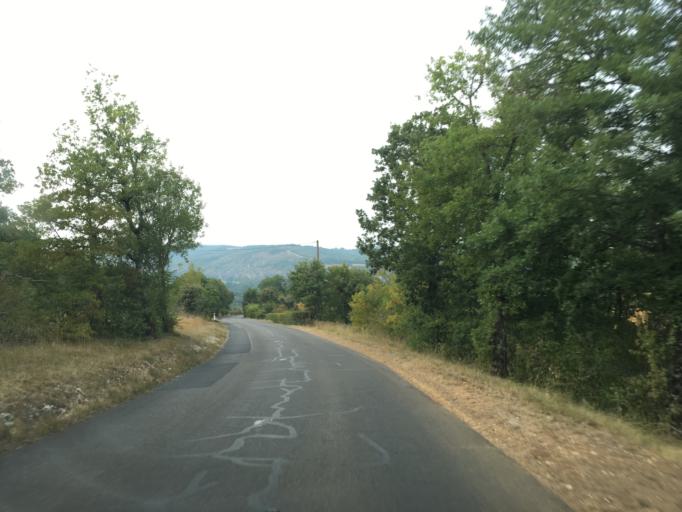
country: FR
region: Midi-Pyrenees
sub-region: Departement du Lot
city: Souillac
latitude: 44.8395
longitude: 1.5592
